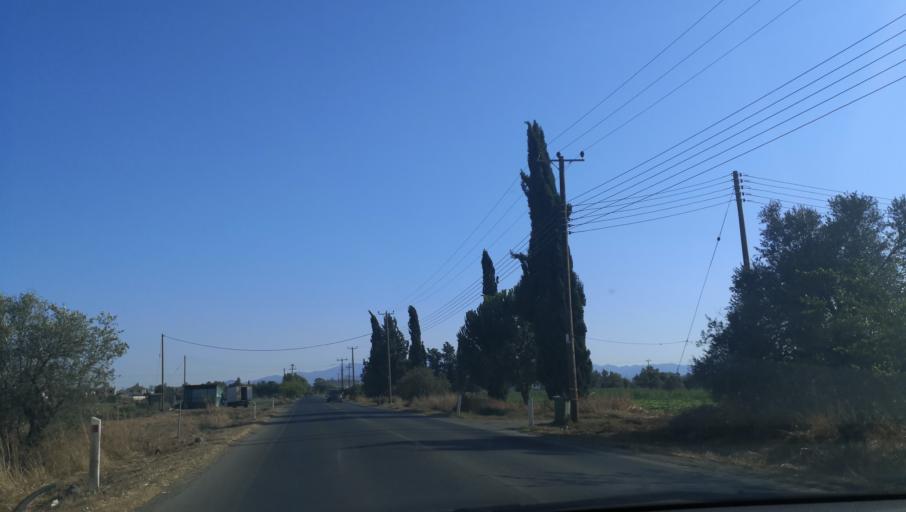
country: CY
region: Lefkosia
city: Psimolofou
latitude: 35.0681
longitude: 33.2676
